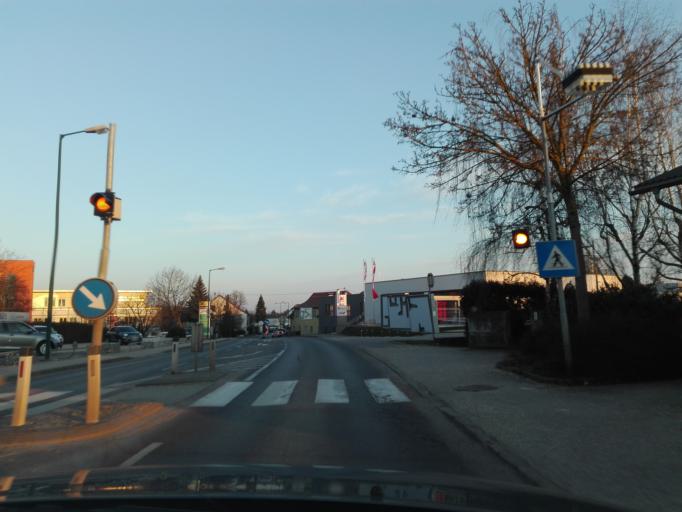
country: AT
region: Upper Austria
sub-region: Politischer Bezirk Urfahr-Umgebung
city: Feldkirchen an der Donau
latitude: 48.3072
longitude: 14.0224
